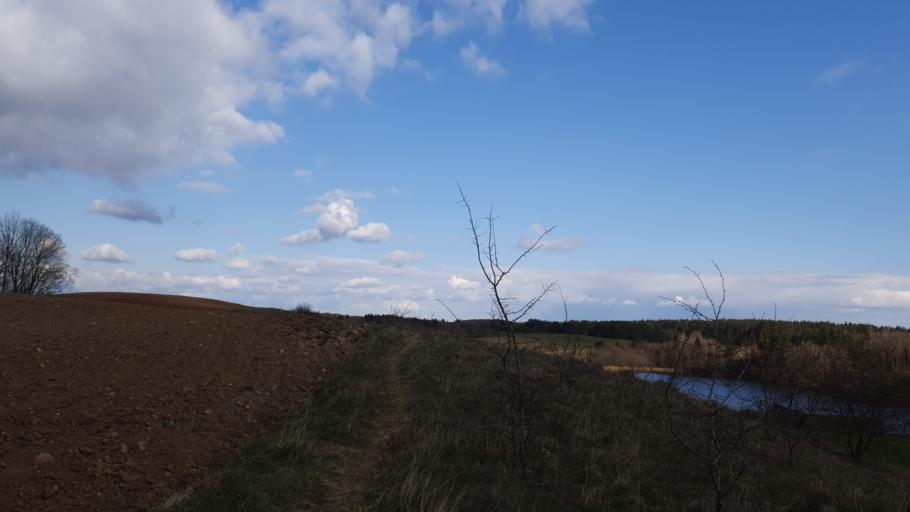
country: LT
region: Vilnius County
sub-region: Trakai
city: Rudiskes
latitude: 54.6124
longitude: 24.7143
